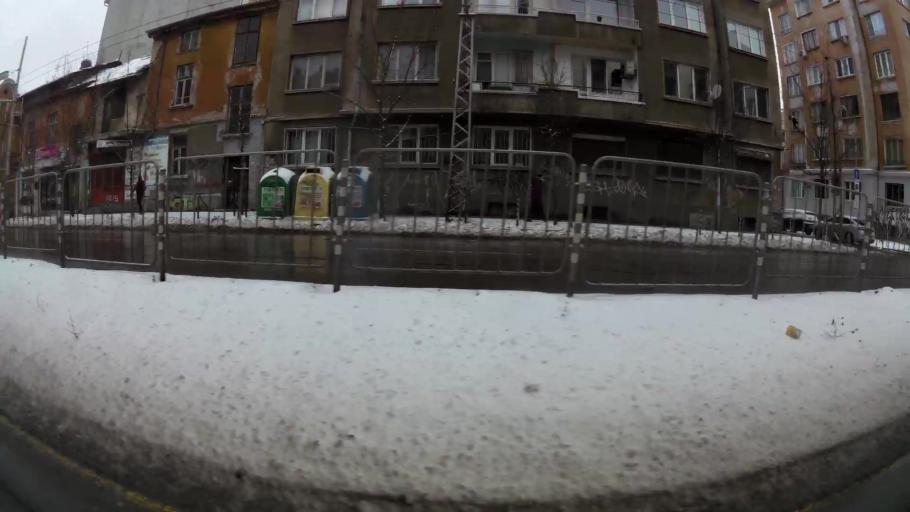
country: BG
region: Sofia-Capital
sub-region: Stolichna Obshtina
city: Sofia
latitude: 42.7034
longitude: 23.3333
